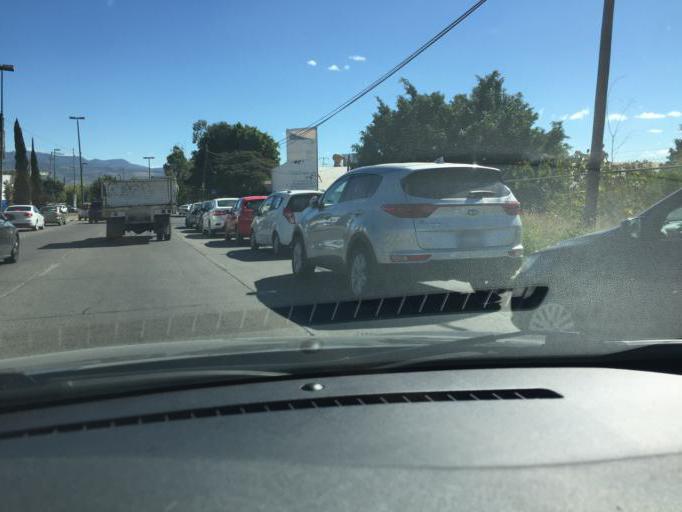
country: MX
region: Guanajuato
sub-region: Leon
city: La Ermita
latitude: 21.1473
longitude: -101.7059
